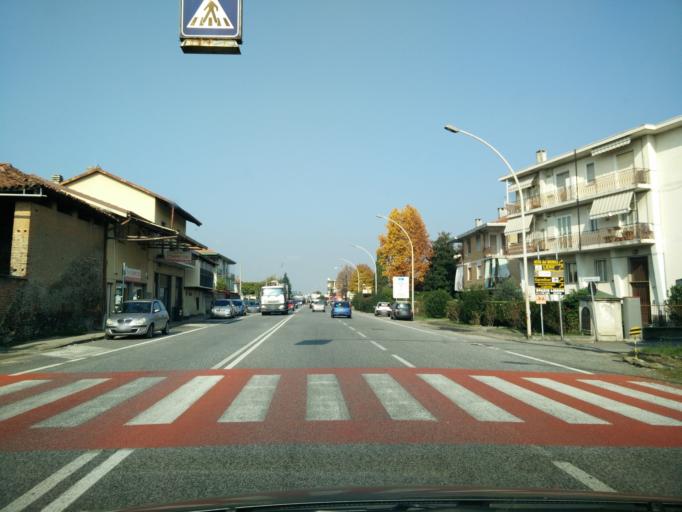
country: IT
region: Piedmont
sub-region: Provincia di Torino
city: Caselle Torinese
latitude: 45.1767
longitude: 7.6504
